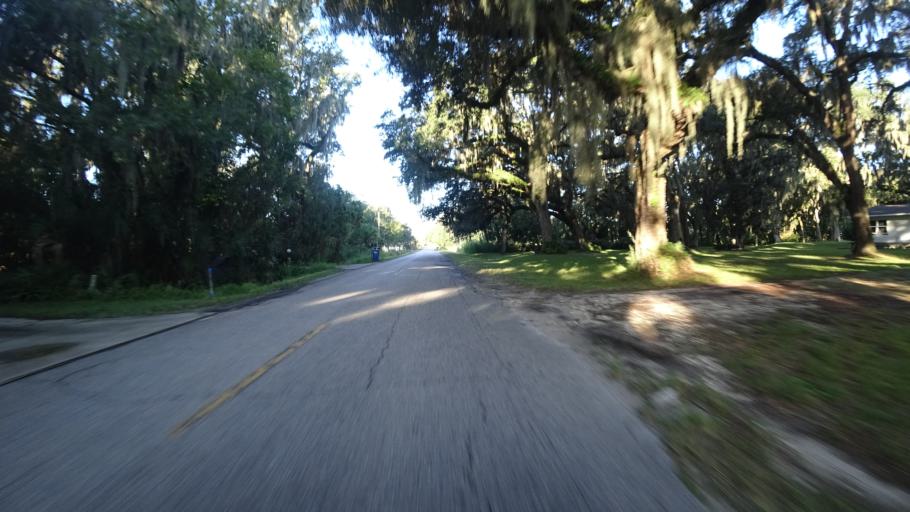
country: US
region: Florida
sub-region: Manatee County
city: Memphis
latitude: 27.5470
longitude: -82.5374
